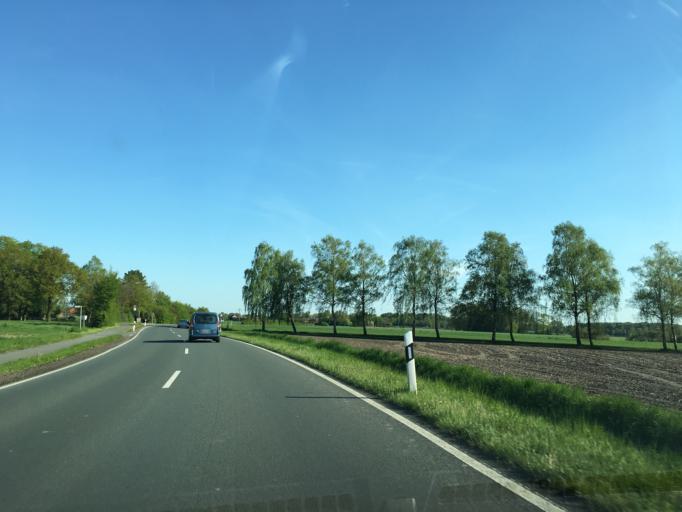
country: DE
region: North Rhine-Westphalia
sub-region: Regierungsbezirk Munster
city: Senden
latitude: 51.8349
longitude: 7.5182
